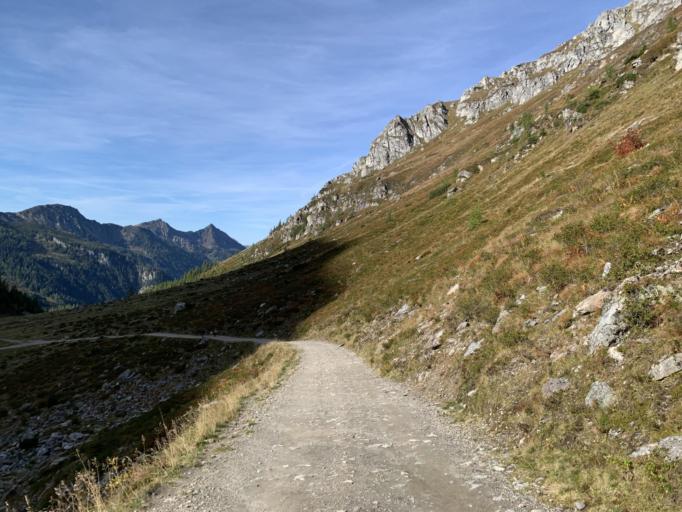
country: AT
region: Salzburg
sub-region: Politischer Bezirk Tamsweg
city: Tweng
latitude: 47.2869
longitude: 13.6354
